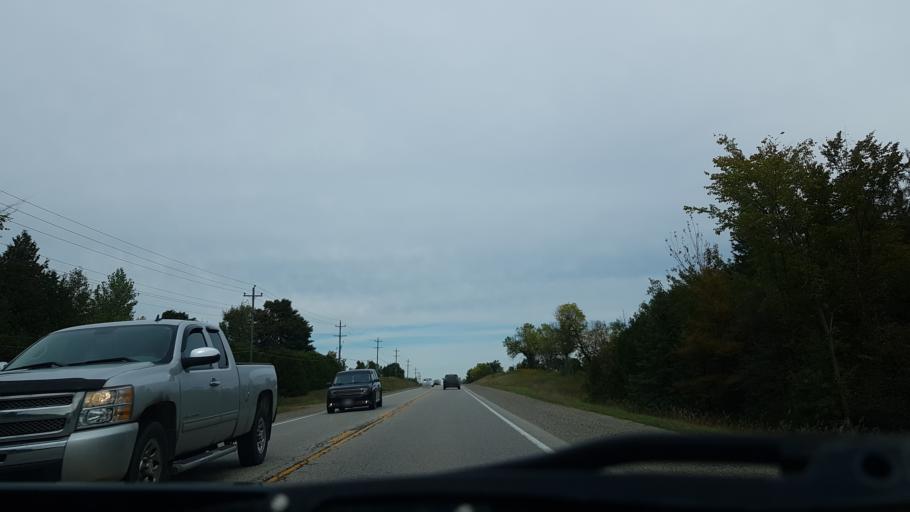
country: CA
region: Ontario
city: Orangeville
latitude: 43.7961
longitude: -80.0664
